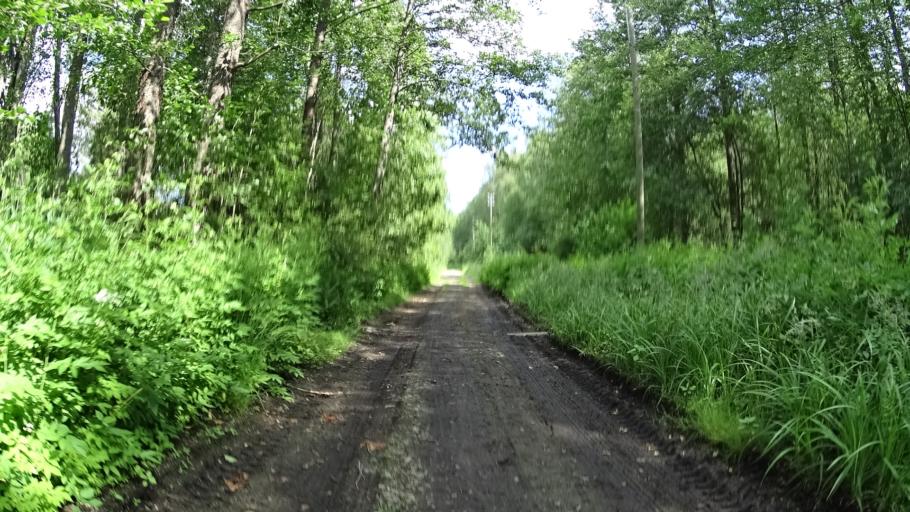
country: FI
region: Uusimaa
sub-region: Raaseporin
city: Pohja
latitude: 60.1037
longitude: 23.5505
